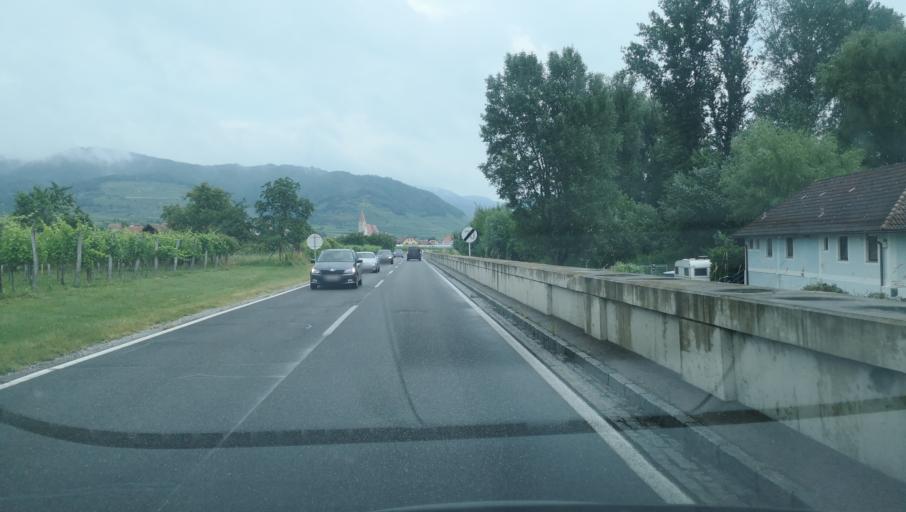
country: AT
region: Lower Austria
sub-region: Politischer Bezirk Krems
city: Weinzierl am Walde
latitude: 48.3882
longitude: 15.4630
